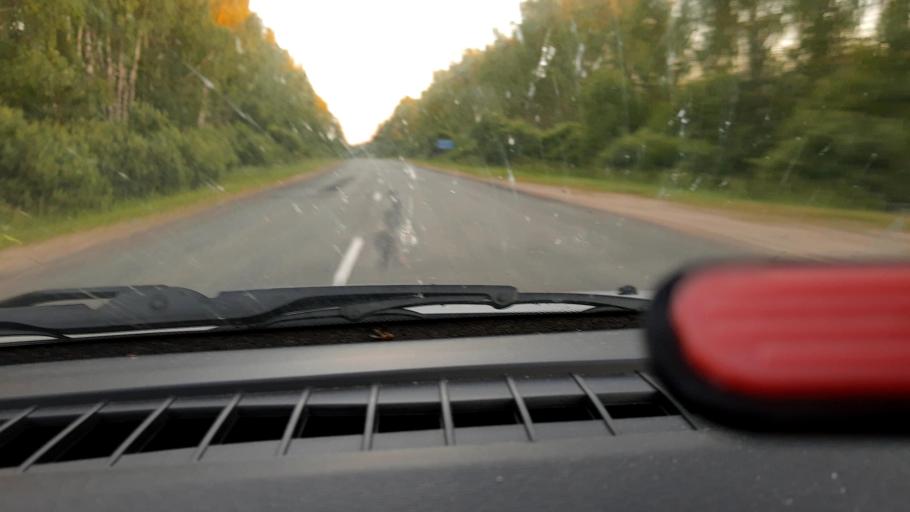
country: RU
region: Nizjnij Novgorod
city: Tonkino
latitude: 57.3076
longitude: 46.4650
